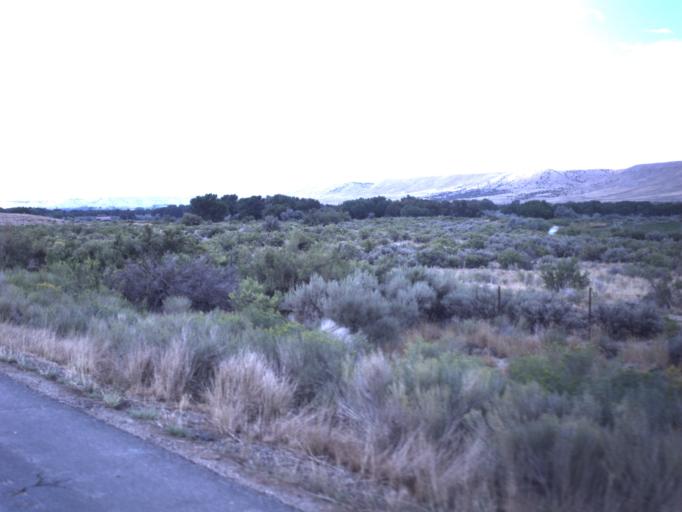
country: US
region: Utah
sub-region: Duchesne County
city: Duchesne
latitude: 40.1530
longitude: -110.2398
